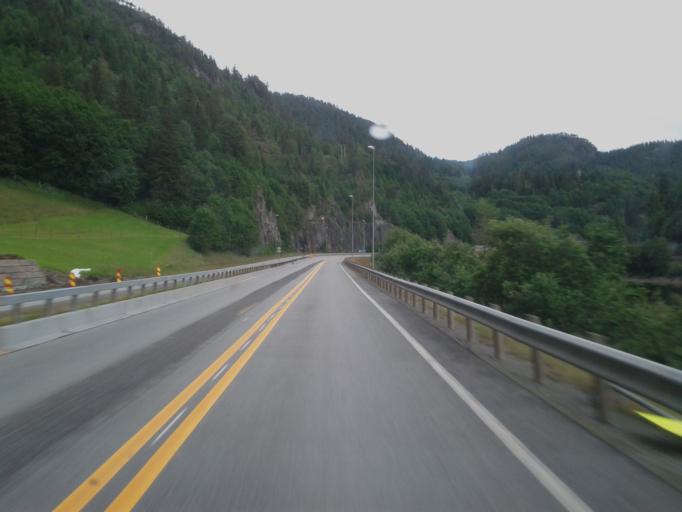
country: NO
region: Sor-Trondelag
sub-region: Midtre Gauldal
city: Storen
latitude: 63.0693
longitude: 10.2785
